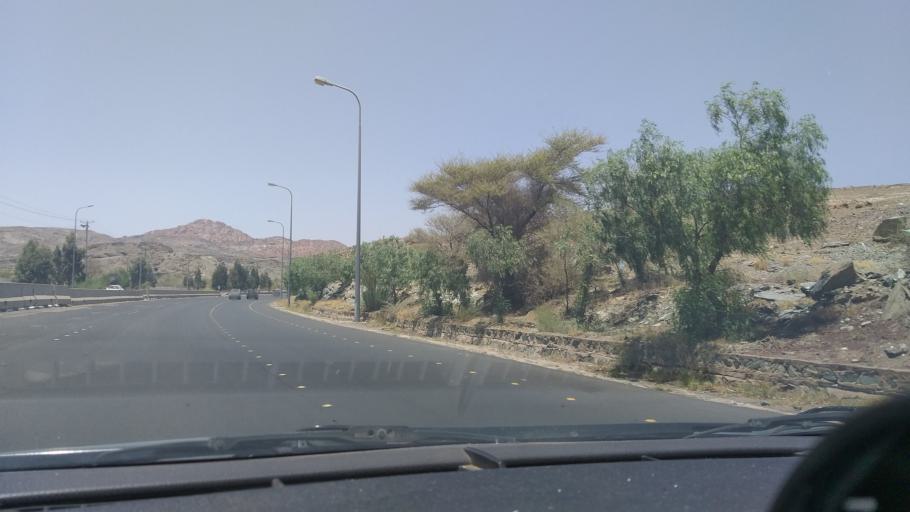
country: SA
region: Makkah
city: Al Hada
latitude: 21.3409
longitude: 40.3342
